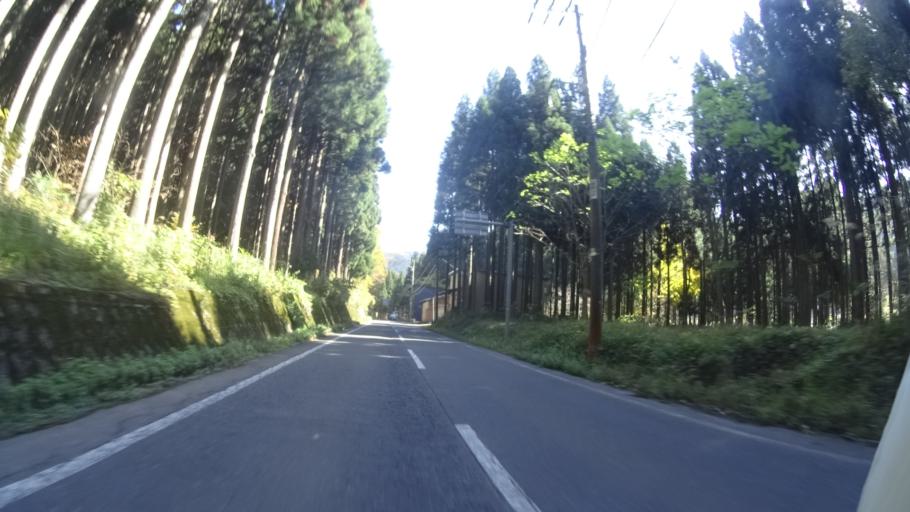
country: JP
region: Fukui
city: Ono
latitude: 35.8776
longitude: 136.3504
